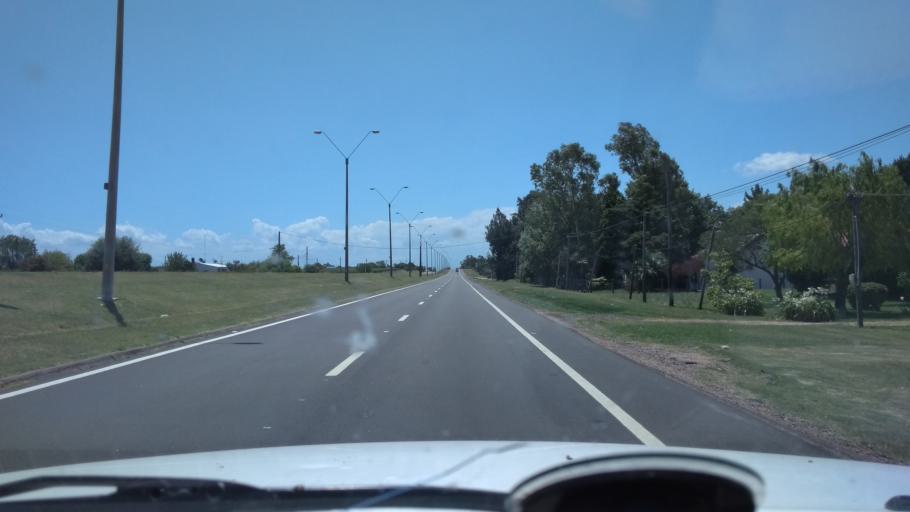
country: UY
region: Canelones
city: Joanico
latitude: -34.5681
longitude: -56.2670
